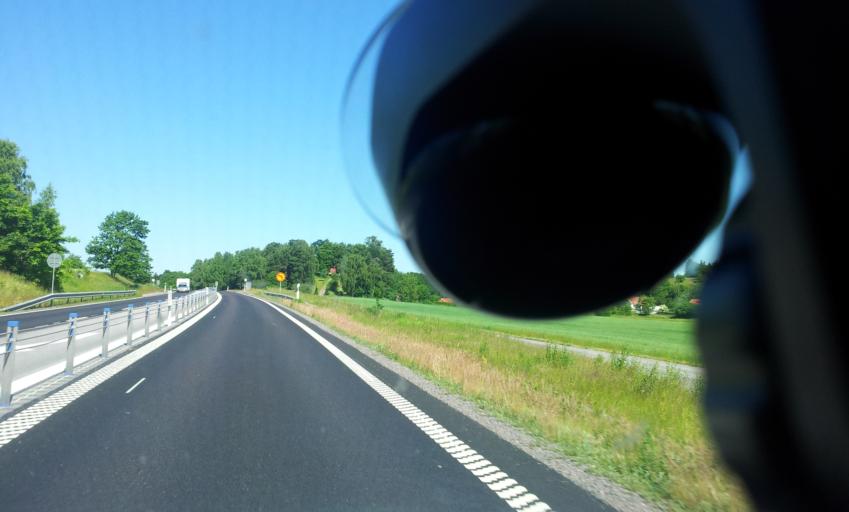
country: SE
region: OEstergoetland
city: Lindo
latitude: 58.5441
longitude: 16.2683
